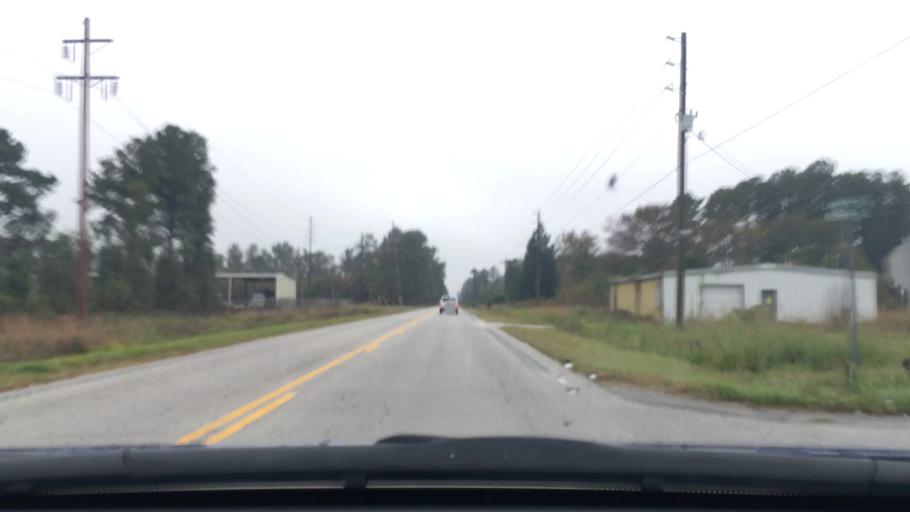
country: US
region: South Carolina
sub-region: Darlington County
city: Darlington
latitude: 34.2706
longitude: -79.9237
